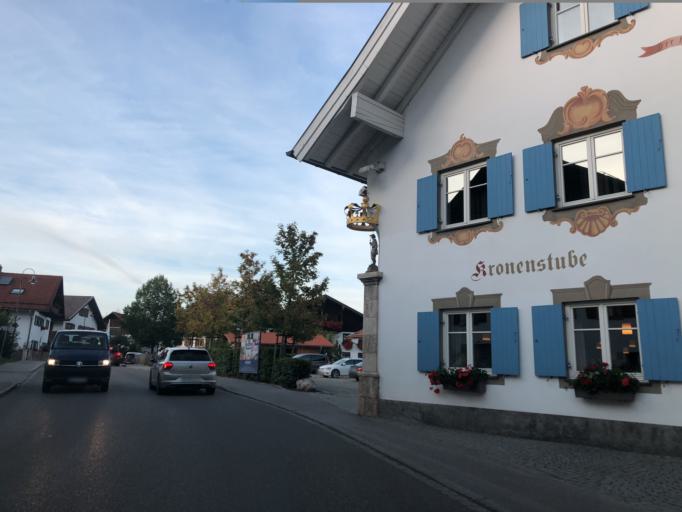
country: DE
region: Bavaria
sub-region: Swabia
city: Pfronten
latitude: 47.5767
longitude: 10.5565
